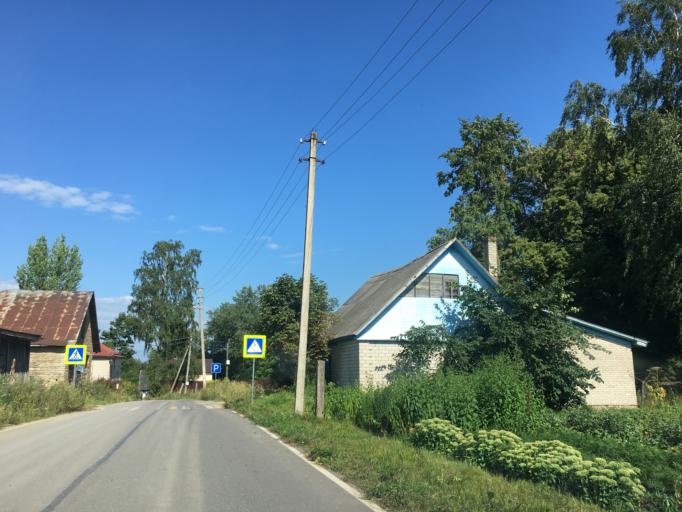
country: RU
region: Pskov
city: Izborsk
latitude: 57.8403
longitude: 27.9930
